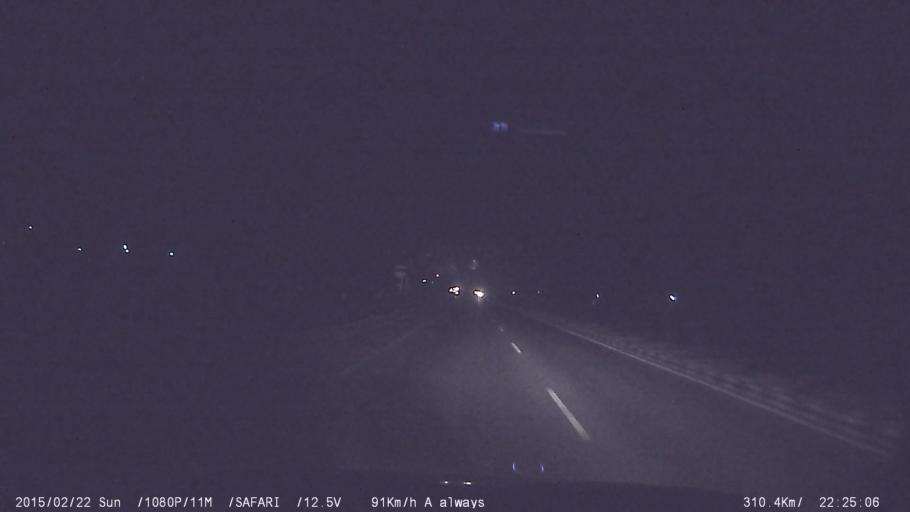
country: IN
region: Tamil Nadu
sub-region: Namakkal
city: Mohanur
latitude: 11.0446
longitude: 78.0568
